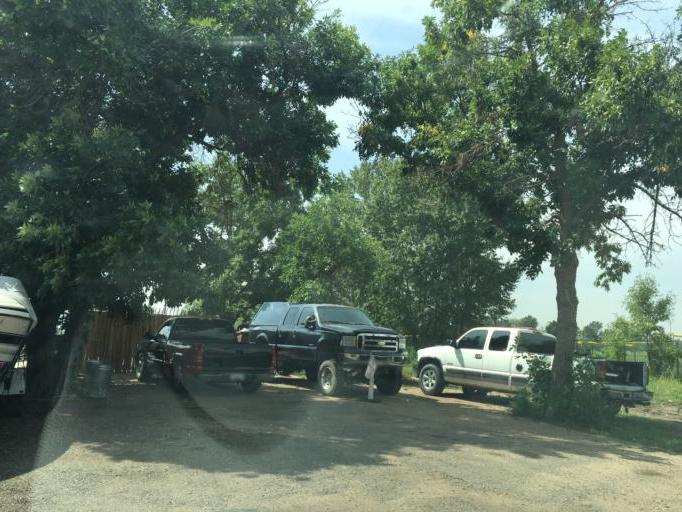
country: US
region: Colorado
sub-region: Adams County
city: Aurora
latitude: 39.7356
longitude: -104.8027
